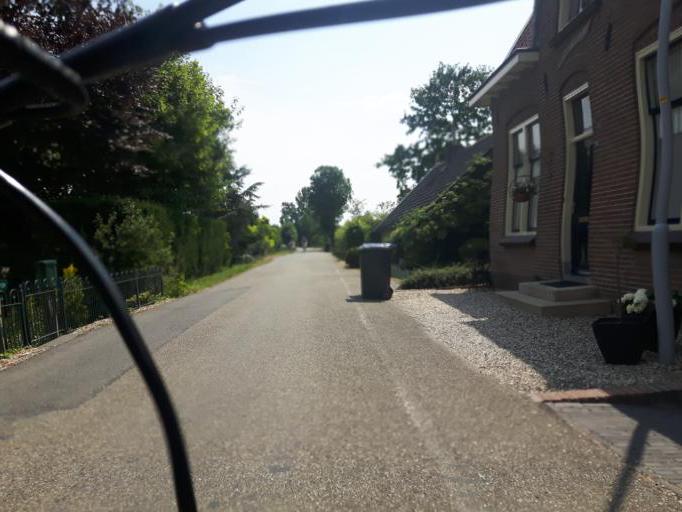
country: NL
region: North Brabant
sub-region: Gemeente Aalburg
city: Aalburg
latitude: 51.8238
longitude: 5.1209
